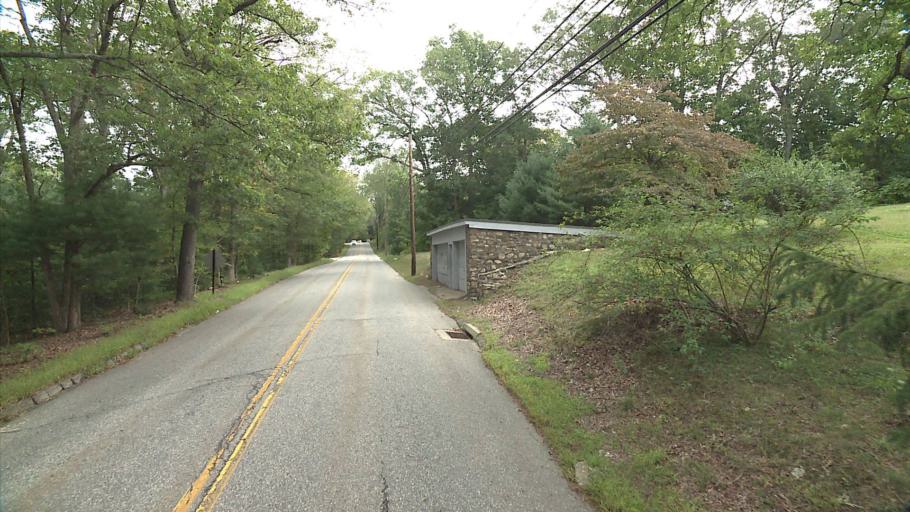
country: US
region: Connecticut
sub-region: Tolland County
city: Storrs
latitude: 41.7876
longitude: -72.2740
